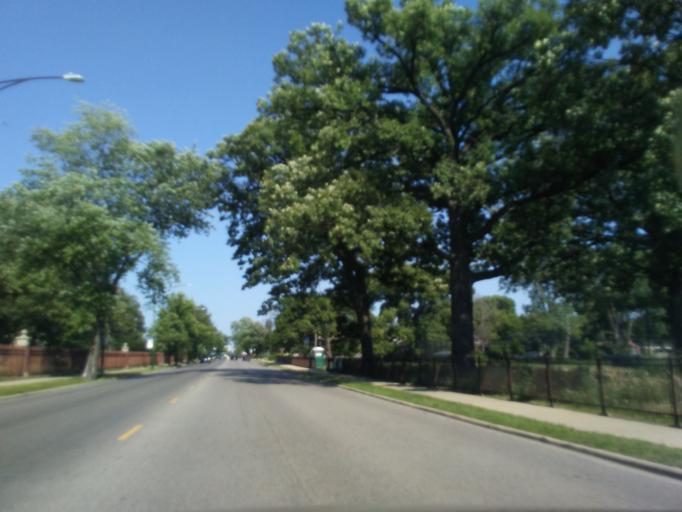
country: US
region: Illinois
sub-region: Cook County
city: Lincolnwood
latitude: 41.9756
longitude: -87.7219
